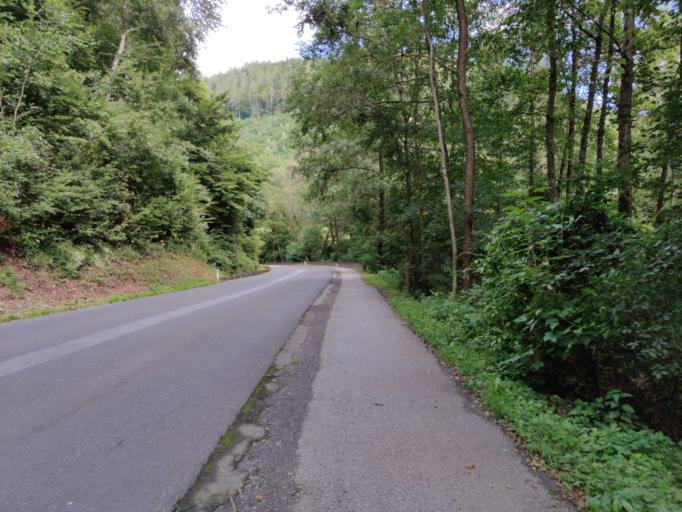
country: AT
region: Styria
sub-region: Politischer Bezirk Graz-Umgebung
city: Thal
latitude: 47.0794
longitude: 15.3633
